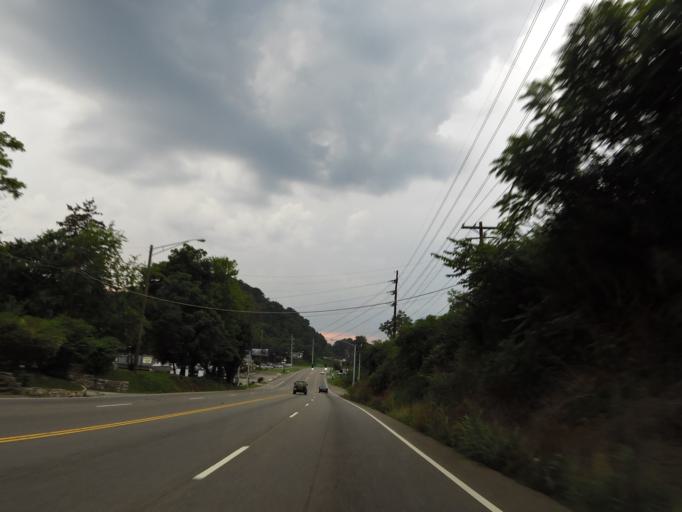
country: US
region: Tennessee
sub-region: Knox County
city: Knoxville
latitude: 35.9276
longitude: -83.8926
